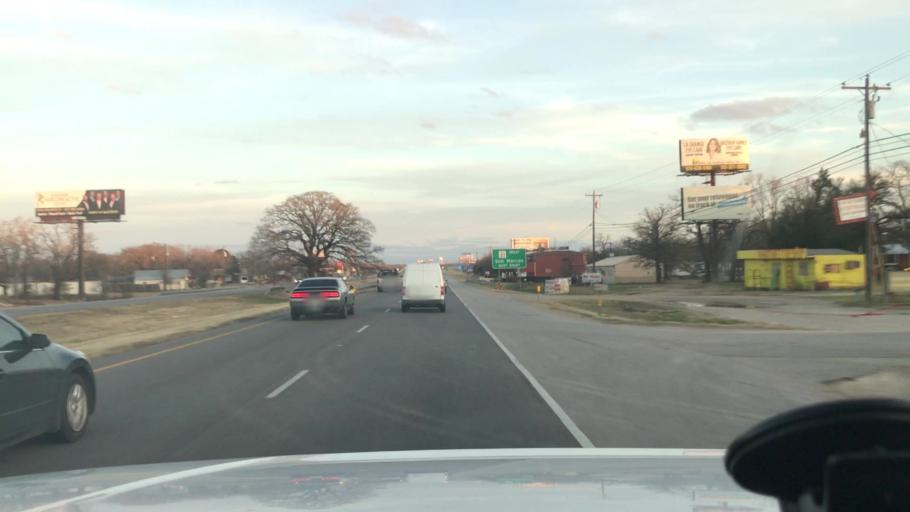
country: US
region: Texas
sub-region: Bastrop County
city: Wyldwood
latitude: 30.1186
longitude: -97.4265
